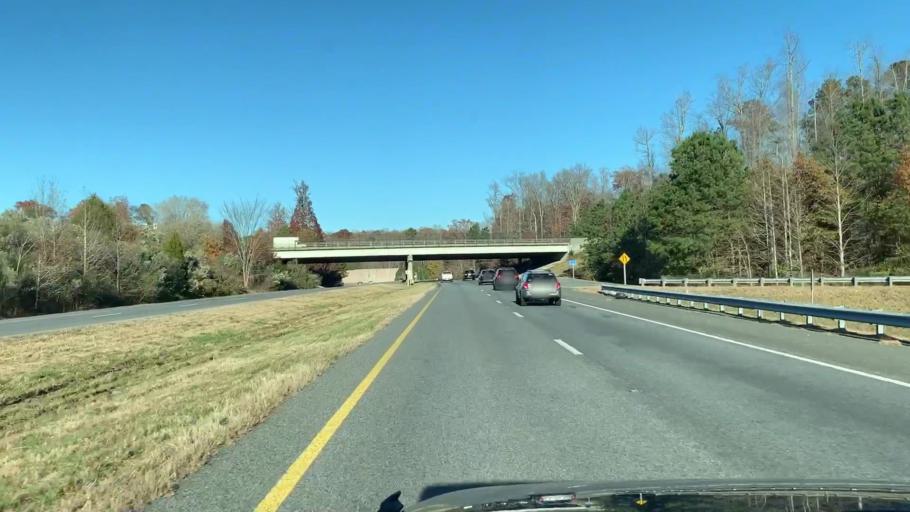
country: US
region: Virginia
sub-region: James City County
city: Williamsburg
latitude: 37.2979
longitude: -76.7468
